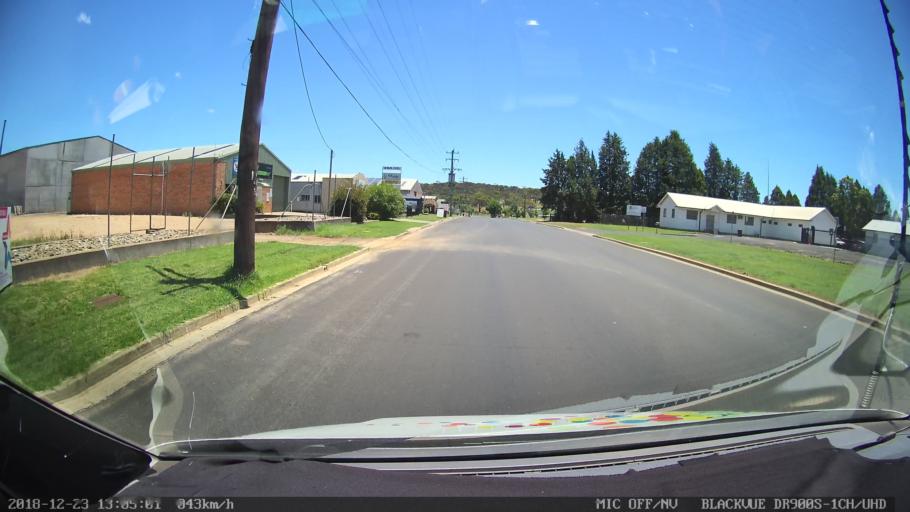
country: AU
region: New South Wales
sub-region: Armidale Dumaresq
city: Armidale
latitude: -30.5153
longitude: 151.6448
